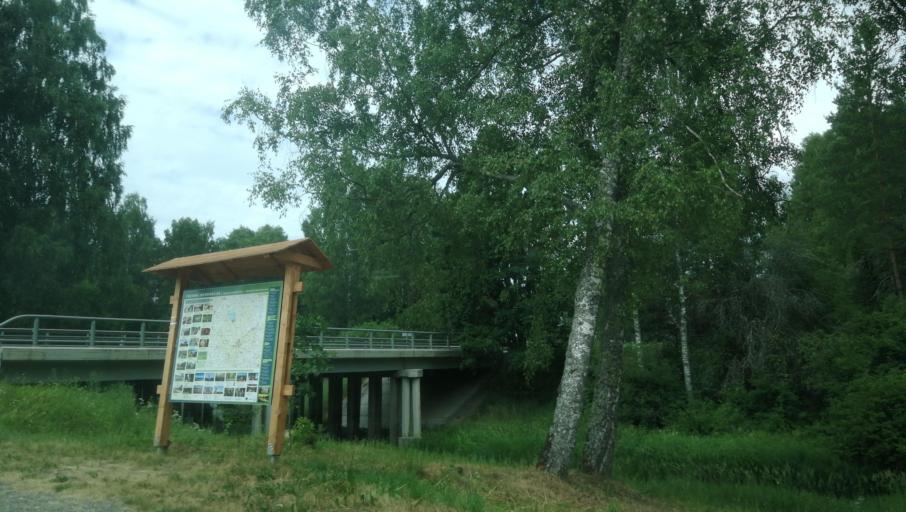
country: LV
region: Naukseni
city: Naukseni
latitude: 57.7868
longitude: 25.4247
